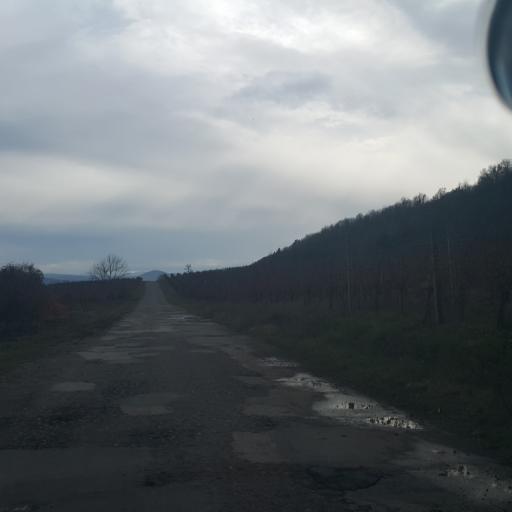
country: RS
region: Central Serbia
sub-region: Zajecarski Okrug
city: Knjazevac
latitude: 43.6182
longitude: 22.2611
